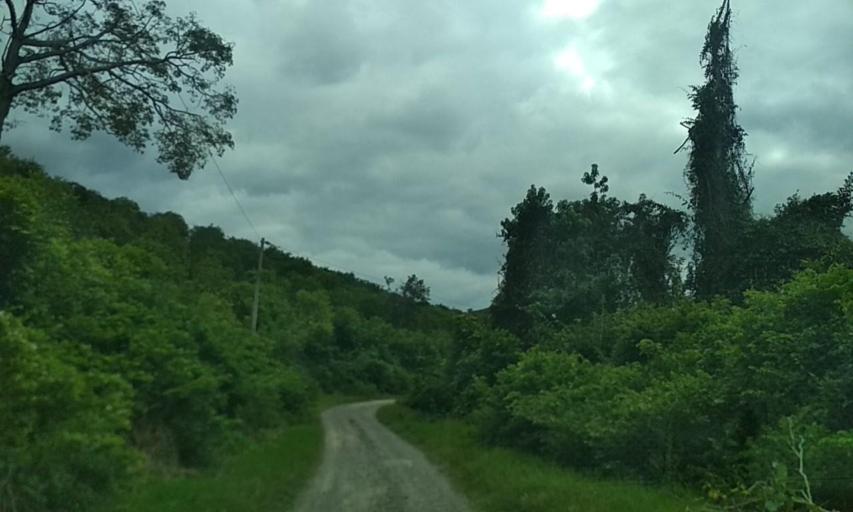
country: MX
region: Veracruz
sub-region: Papantla
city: Polutla
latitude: 20.5302
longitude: -97.2985
